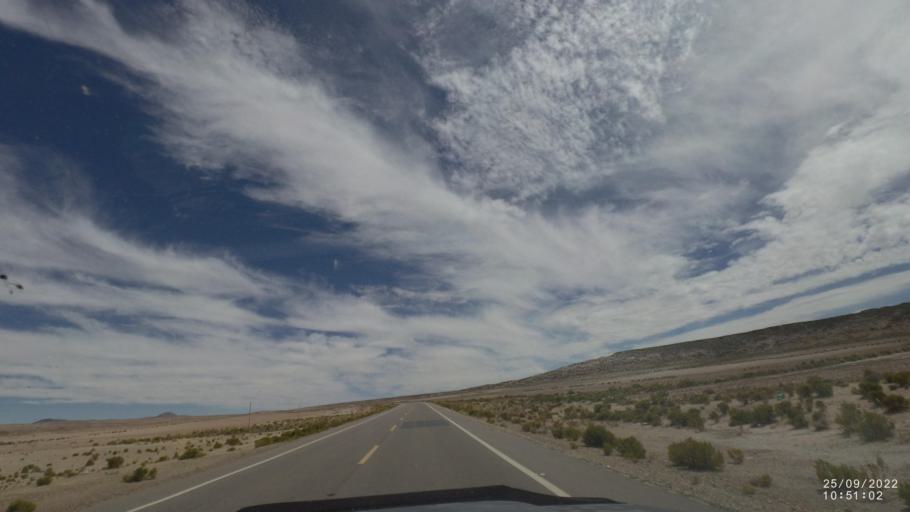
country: BO
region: Oruro
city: Challapata
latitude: -19.5673
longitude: -66.8437
